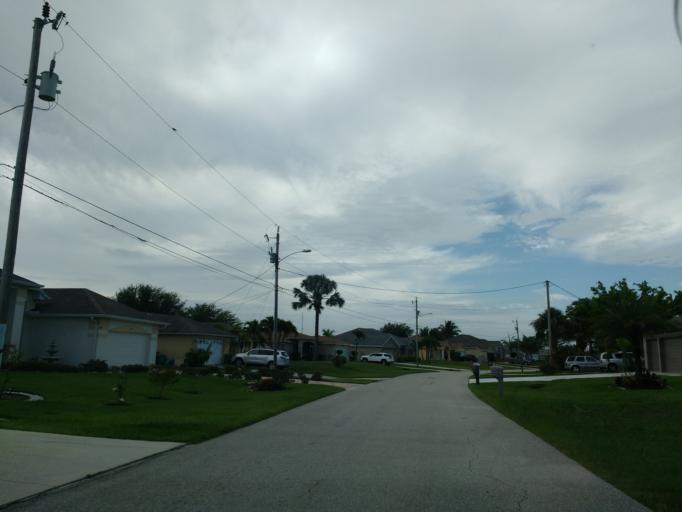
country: US
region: Florida
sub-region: Lee County
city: Cape Coral
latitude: 26.6002
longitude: -82.0248
